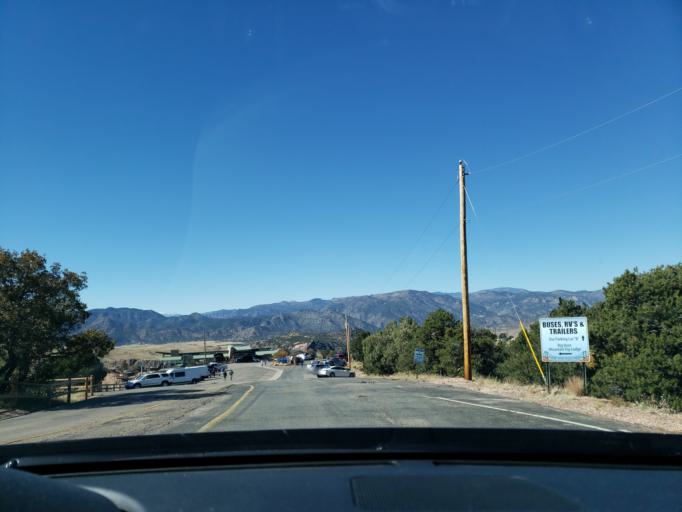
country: US
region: Colorado
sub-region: Fremont County
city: Canon City
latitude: 38.4633
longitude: -105.3187
